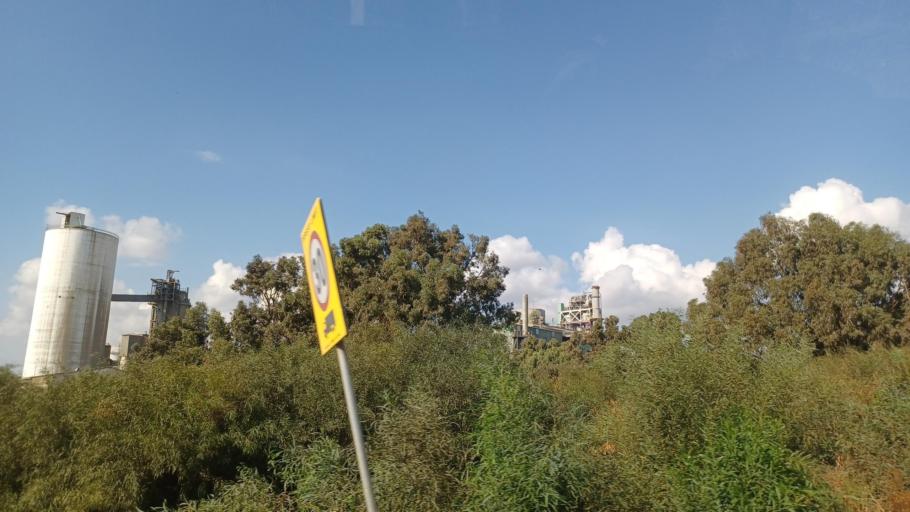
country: CY
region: Larnaka
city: Kofinou
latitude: 34.7207
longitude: 33.3199
